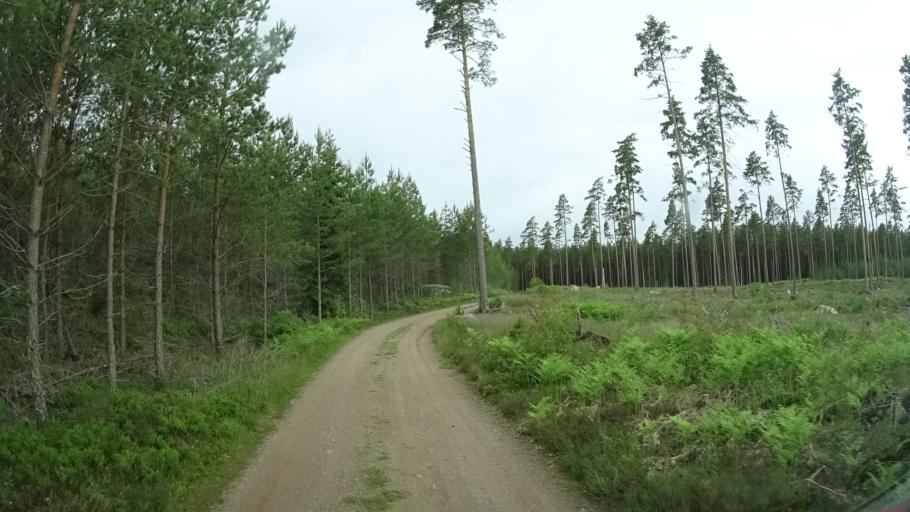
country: SE
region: Kalmar
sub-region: Vimmerby Kommun
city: Sodra Vi
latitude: 57.7155
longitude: 15.7781
